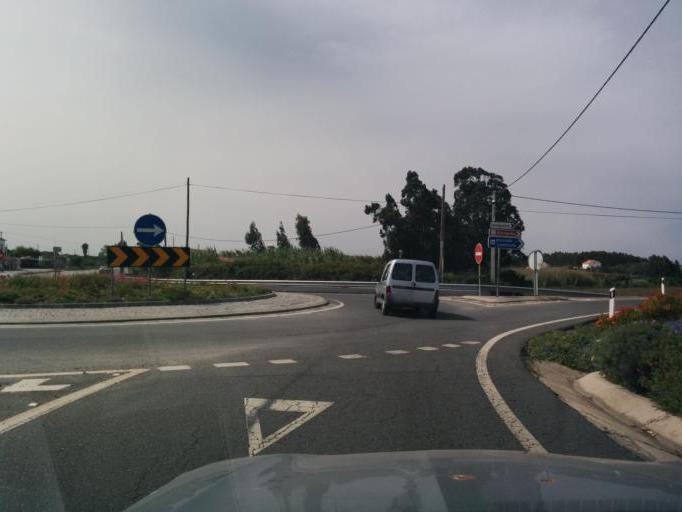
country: PT
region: Beja
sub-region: Odemira
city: Vila Nova de Milfontes
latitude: 37.6558
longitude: -8.7597
